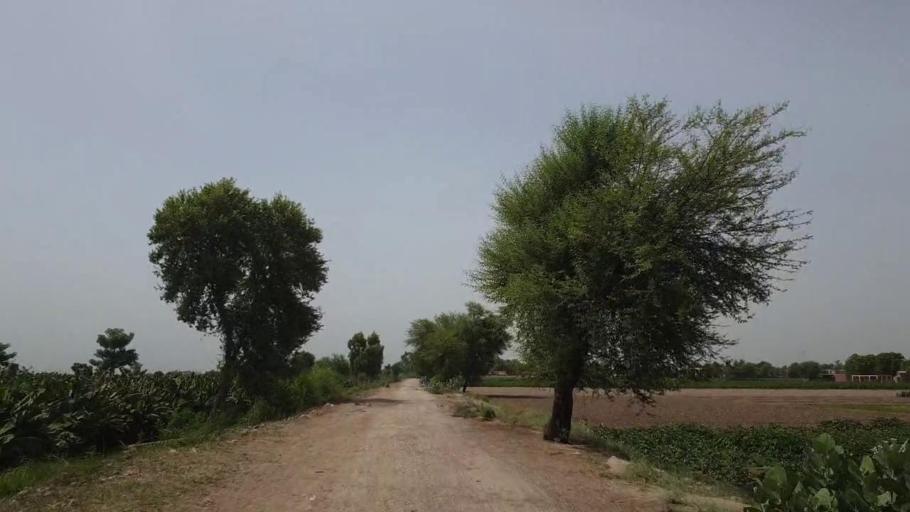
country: PK
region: Sindh
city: Sakrand
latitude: 26.1308
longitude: 68.2865
